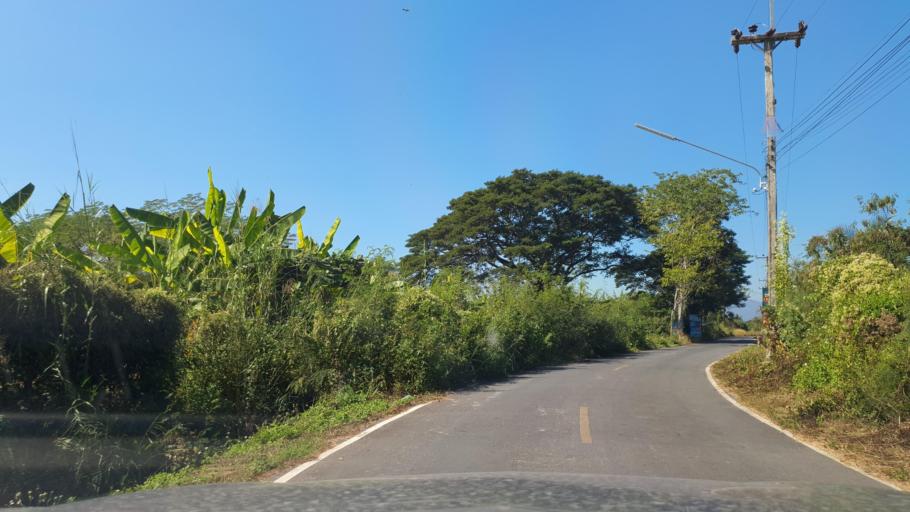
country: TH
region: Chiang Mai
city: San Pa Tong
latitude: 18.6498
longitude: 98.8946
